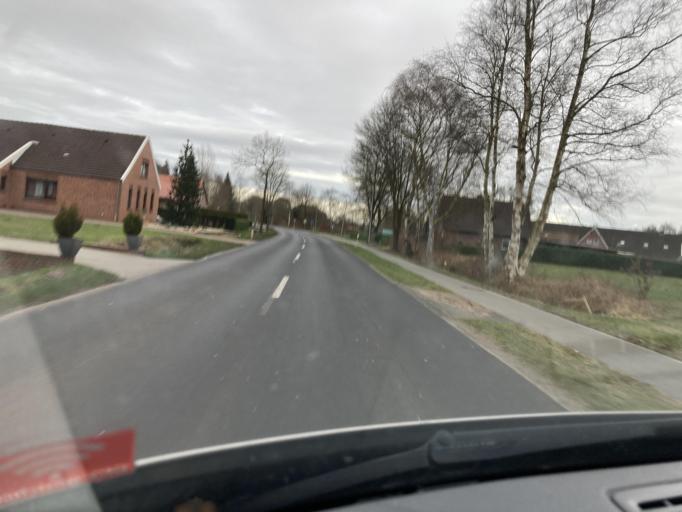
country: DE
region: Lower Saxony
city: Papenburg
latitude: 53.1318
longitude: 7.4793
